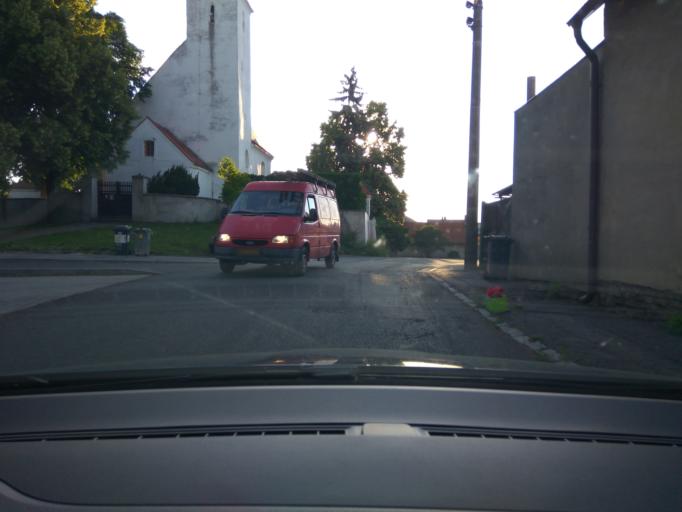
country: CZ
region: Central Bohemia
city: Hovorcovice
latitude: 50.1790
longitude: 14.5184
